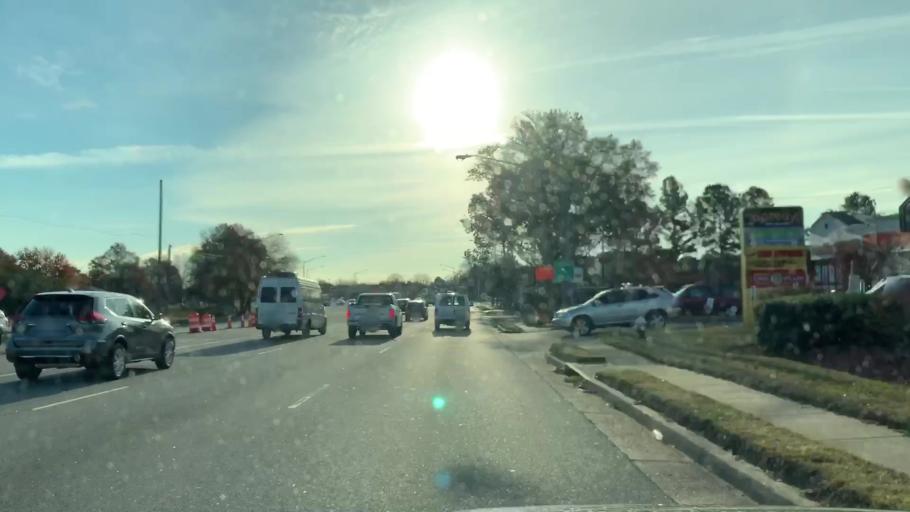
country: US
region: Virginia
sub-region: City of Chesapeake
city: Chesapeake
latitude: 36.7964
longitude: -76.1736
